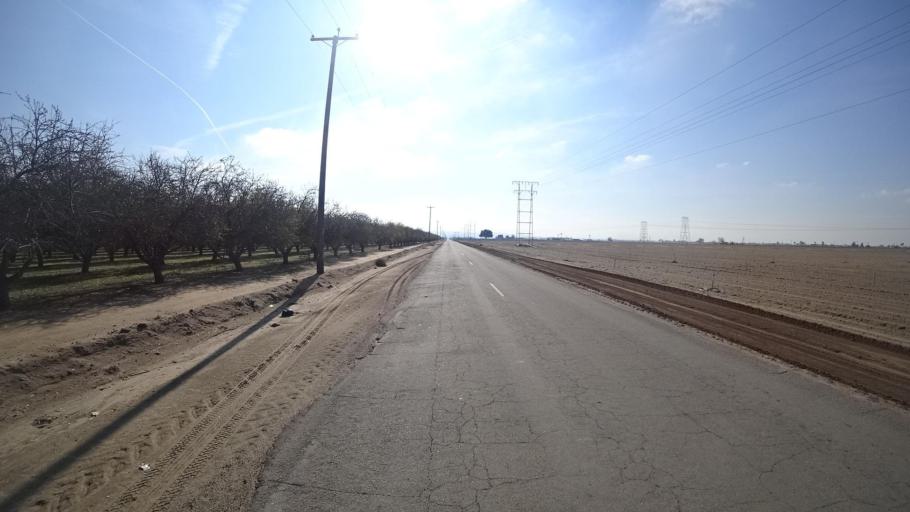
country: US
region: California
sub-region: Kern County
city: Arvin
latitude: 35.2351
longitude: -118.8064
